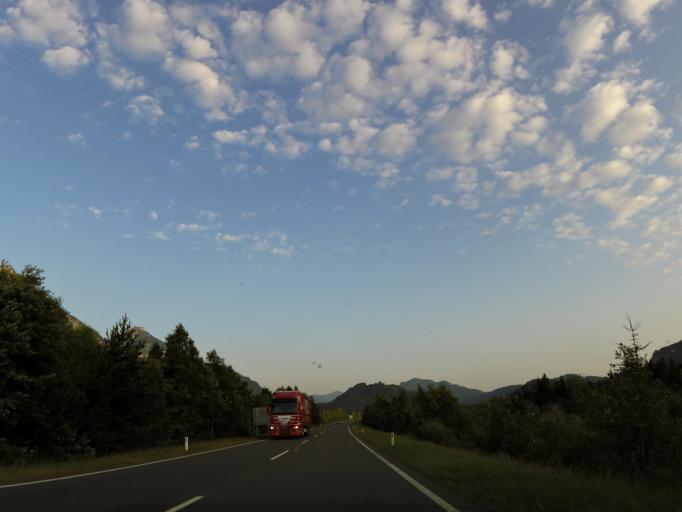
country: AT
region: Tyrol
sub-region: Politischer Bezirk Reutte
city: Pflach
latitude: 47.5275
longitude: 10.6935
